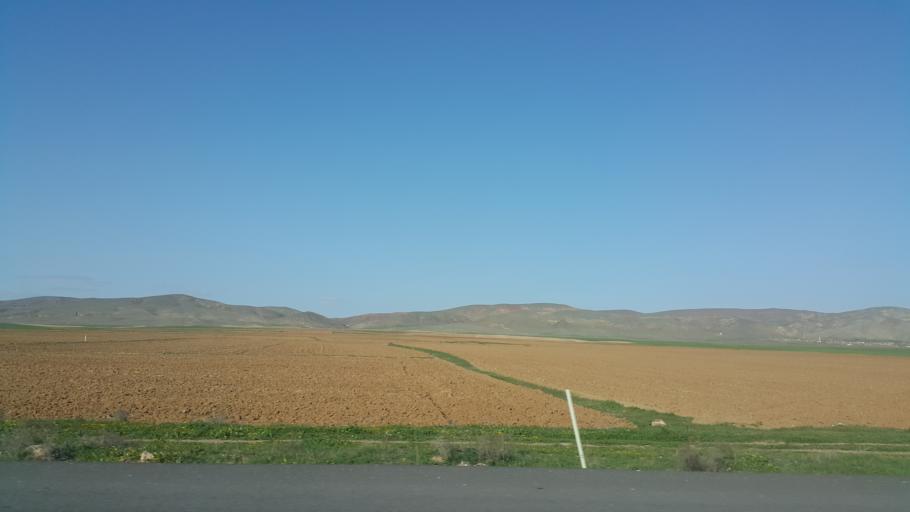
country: TR
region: Aksaray
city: Acipinar
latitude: 38.6683
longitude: 33.7103
